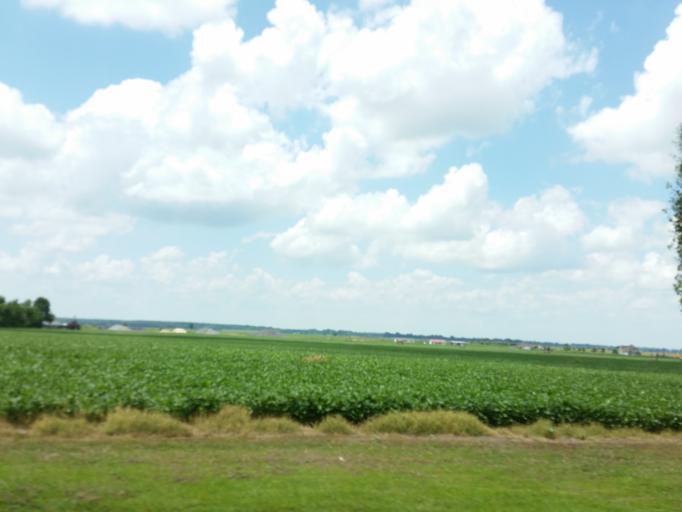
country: US
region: Tennessee
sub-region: Lake County
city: Ridgely
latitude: 36.2737
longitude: -89.4778
